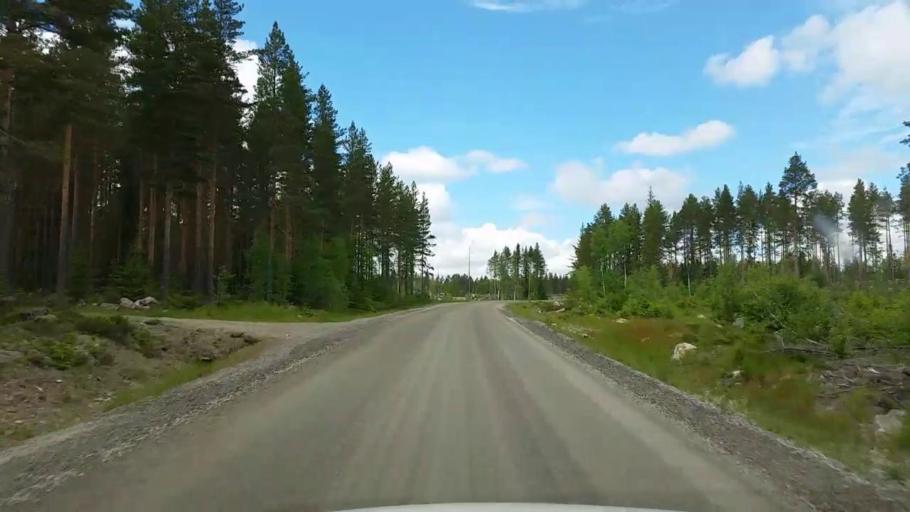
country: SE
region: Gaevleborg
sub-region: Bollnas Kommun
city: Kilafors
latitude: 61.0026
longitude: 16.3890
